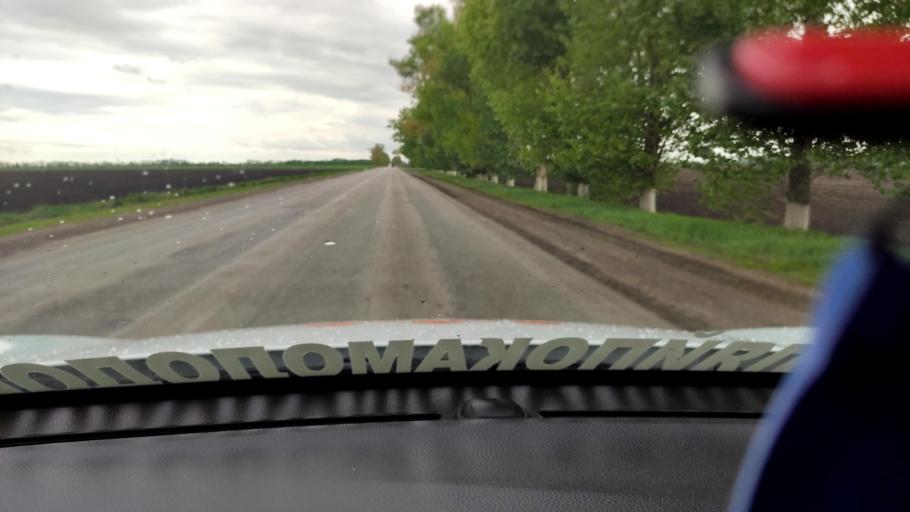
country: RU
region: Voronezj
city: Liski
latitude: 51.0326
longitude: 39.6171
